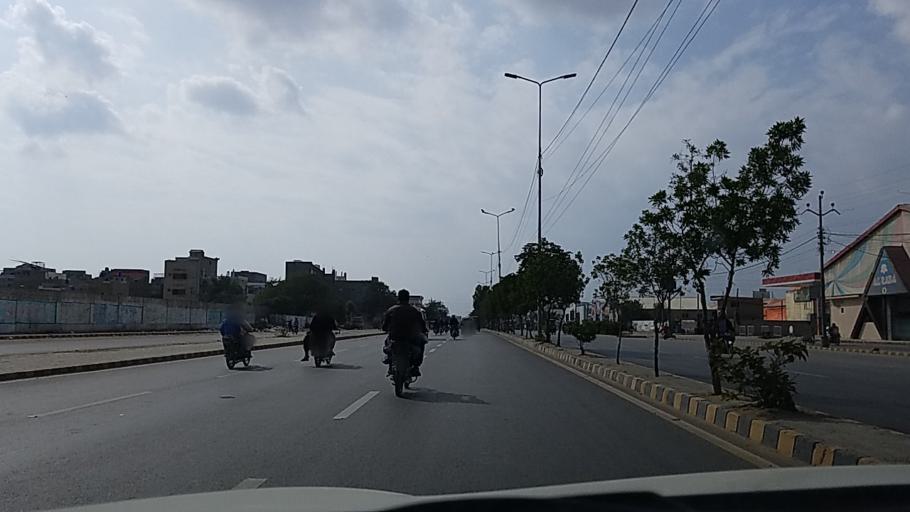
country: PK
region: Sindh
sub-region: Karachi District
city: Karachi
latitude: 24.8200
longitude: 67.1229
